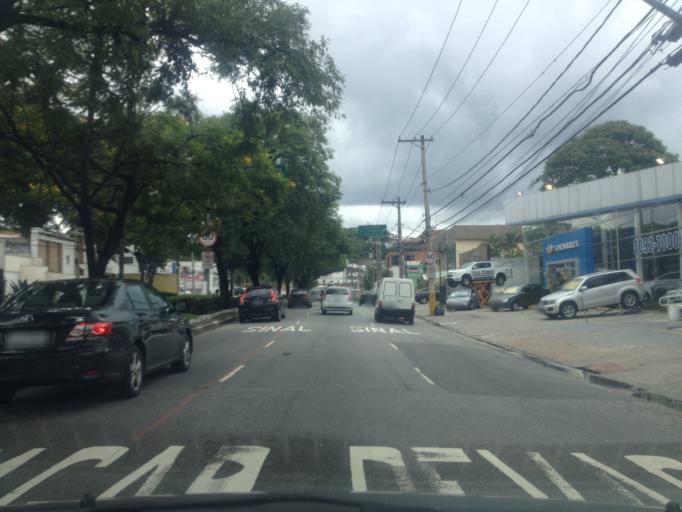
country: BR
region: Sao Paulo
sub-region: Sao Paulo
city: Sao Paulo
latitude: -23.5863
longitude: -46.6958
